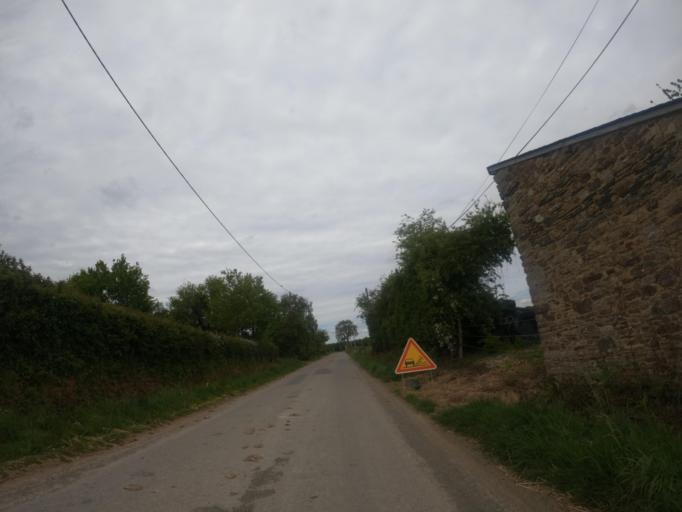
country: FR
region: Pays de la Loire
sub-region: Departement de la Loire-Atlantique
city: Rouge
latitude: 47.7361
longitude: -1.4437
